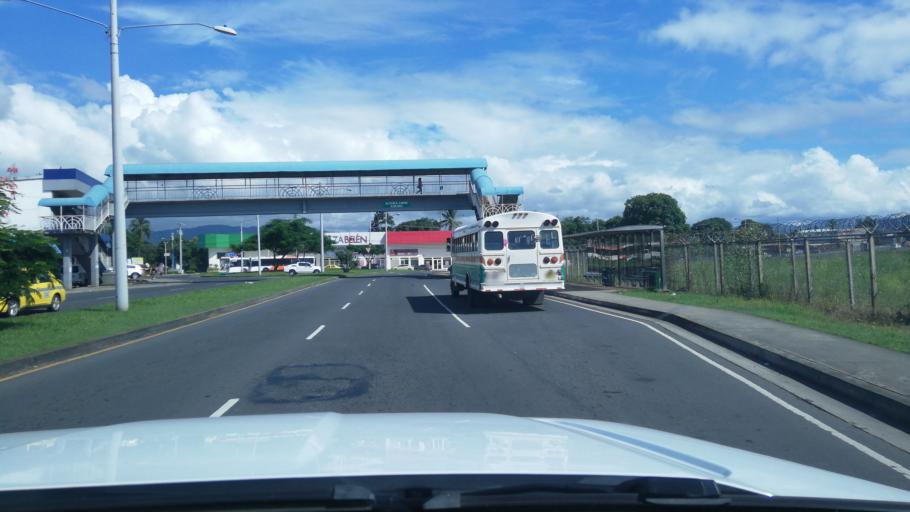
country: PA
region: Panama
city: Tocumen
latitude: 9.0859
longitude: -79.3842
